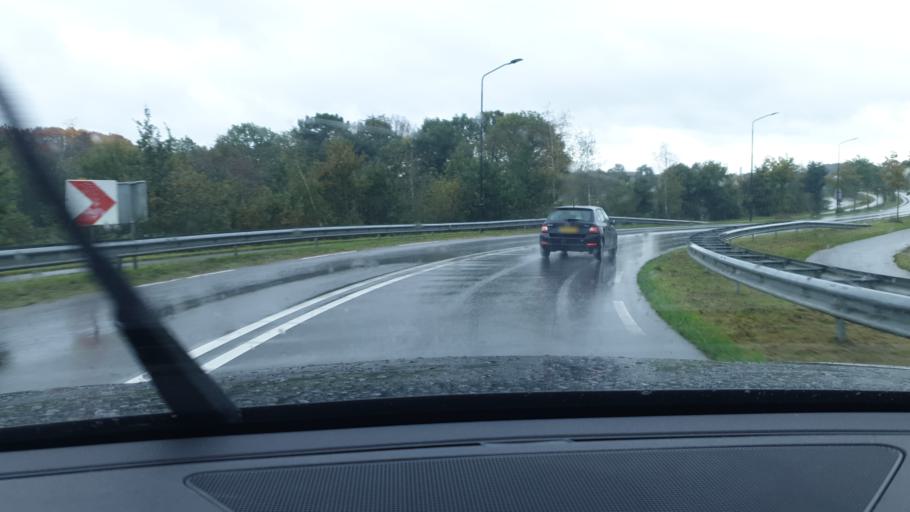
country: NL
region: North Brabant
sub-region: Gemeente Uden
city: Uden
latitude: 51.6808
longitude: 5.5967
